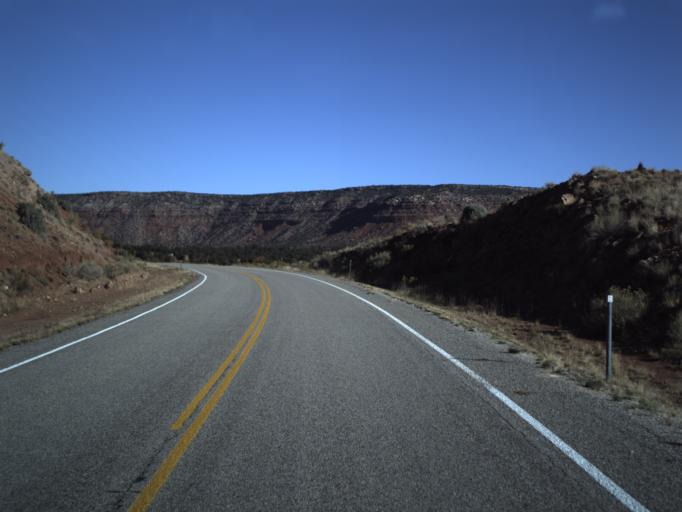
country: US
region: Utah
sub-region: San Juan County
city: Blanding
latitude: 37.5857
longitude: -110.0398
